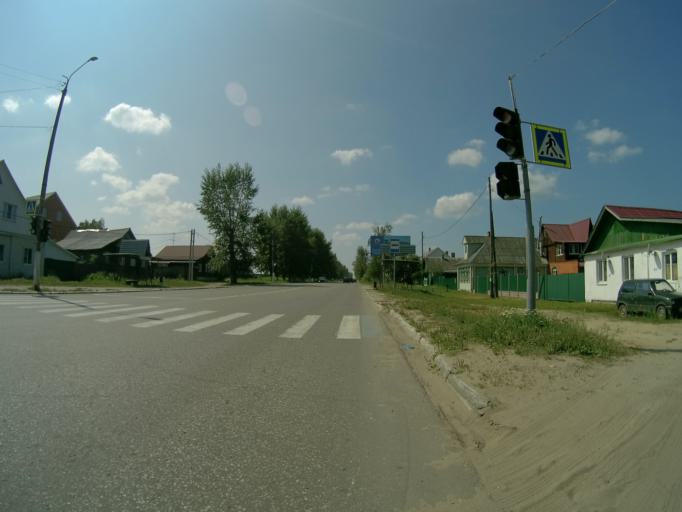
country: RU
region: Vladimir
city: Gus'-Khrustal'nyy
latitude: 55.6268
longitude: 40.6862
